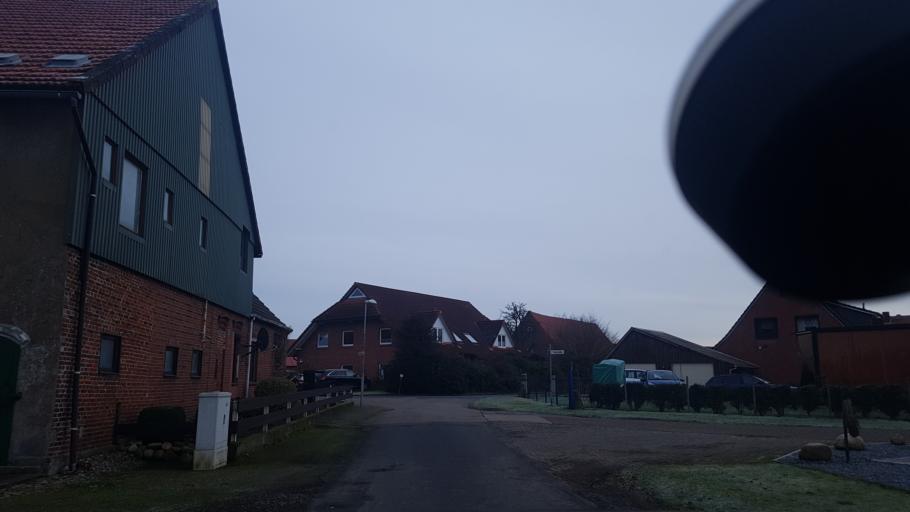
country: DE
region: Lower Saxony
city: Elmlohe
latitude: 53.6088
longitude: 8.6790
